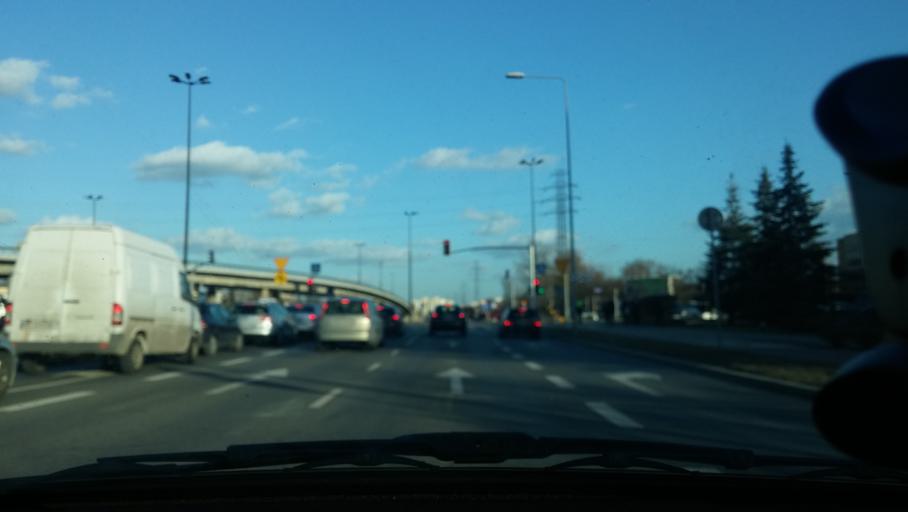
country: PL
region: Masovian Voivodeship
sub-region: Warszawa
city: Ursynow
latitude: 52.1530
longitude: 21.0163
